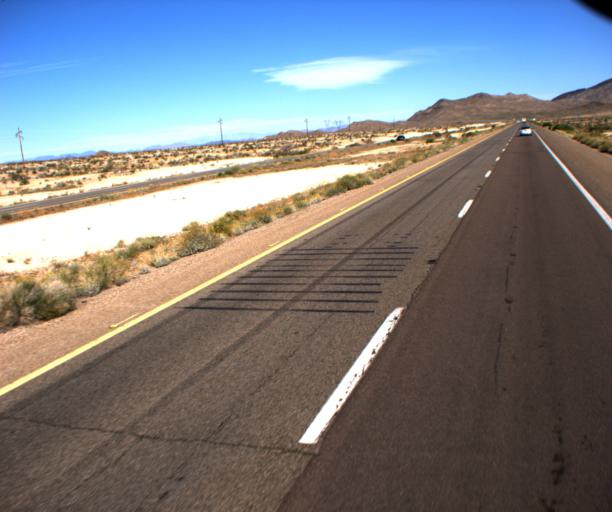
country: US
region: Nevada
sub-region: Clark County
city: Boulder City
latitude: 35.8289
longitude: -114.5602
